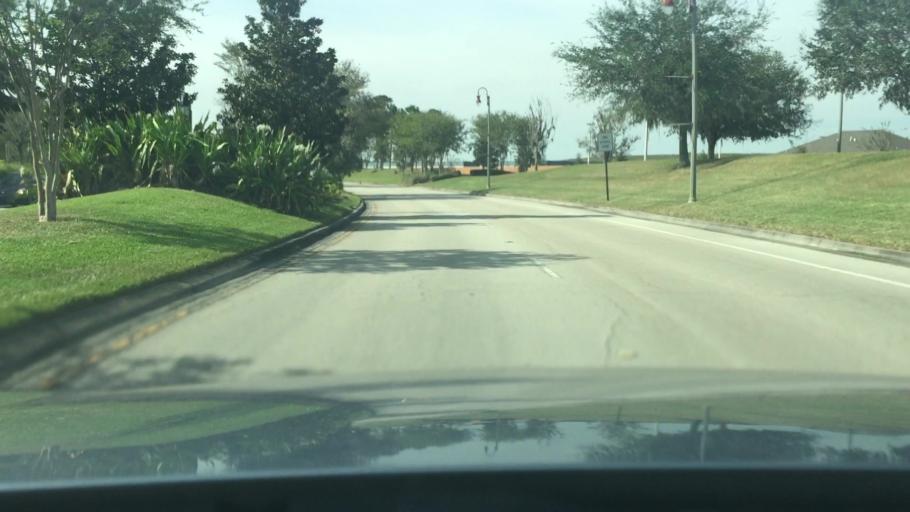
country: US
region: Florida
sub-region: Osceola County
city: Saint Cloud
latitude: 28.2277
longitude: -81.3023
